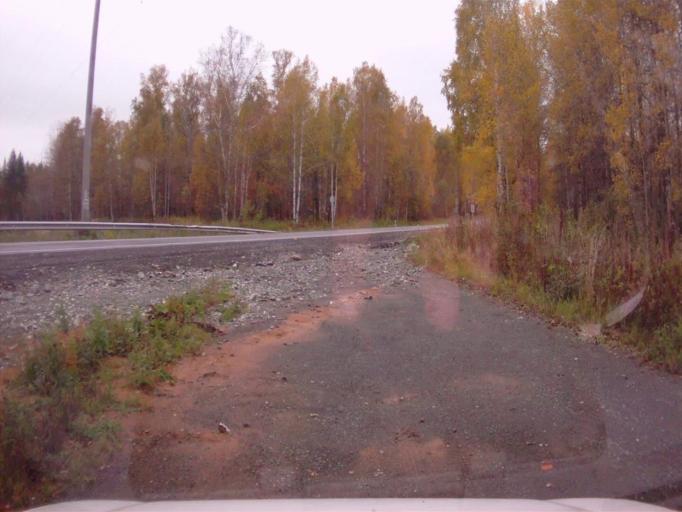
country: RU
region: Chelyabinsk
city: Nyazepetrovsk
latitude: 56.0657
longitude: 59.6556
